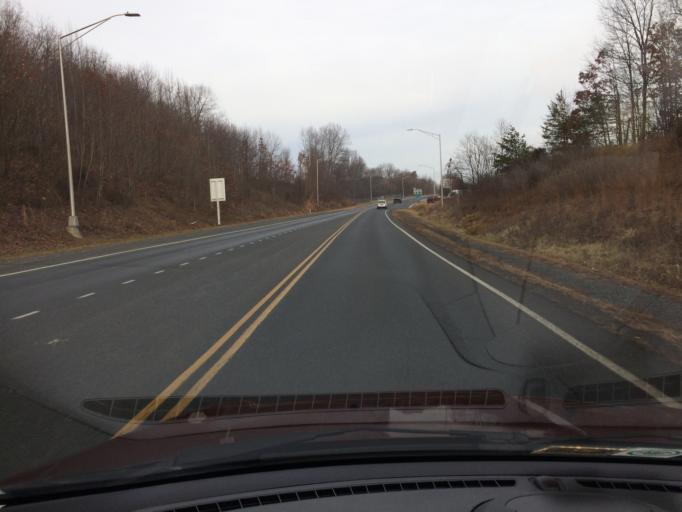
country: US
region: Virginia
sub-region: City of Bedford
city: Bedford
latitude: 37.3435
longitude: -79.5017
